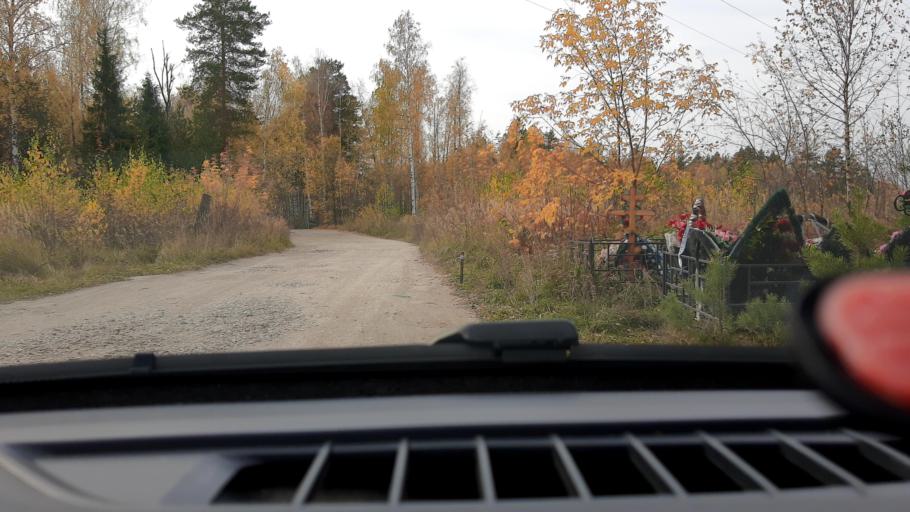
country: RU
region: Nizjnij Novgorod
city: Gorbatovka
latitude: 56.2861
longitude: 43.8215
